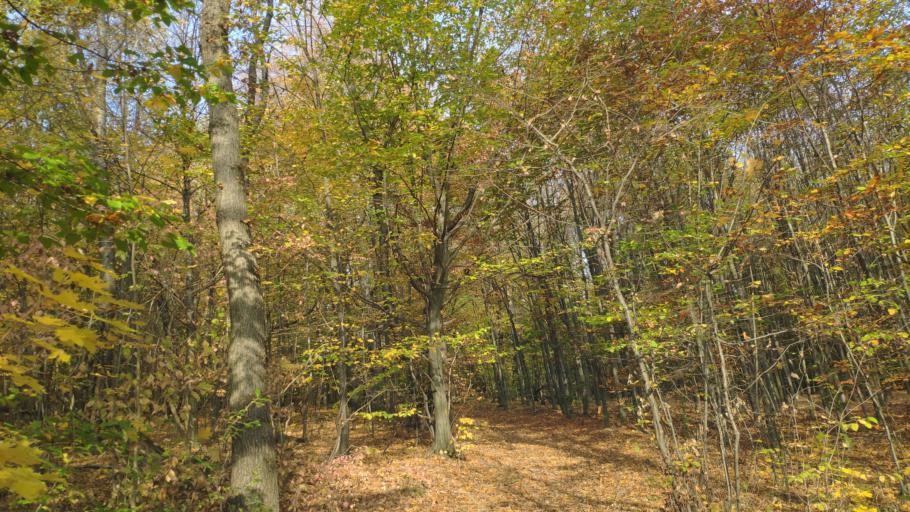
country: SK
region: Kosicky
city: Kosice
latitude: 48.7449
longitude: 21.2271
